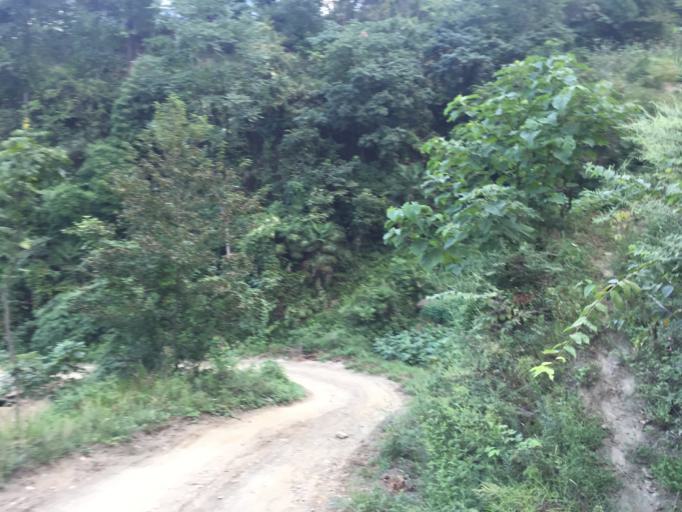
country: CN
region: Guizhou Sheng
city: Shiqian
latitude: 27.6107
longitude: 107.9967
